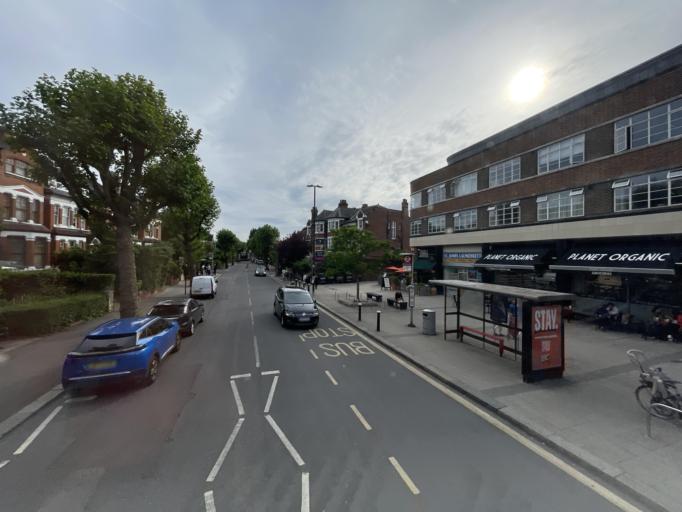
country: GB
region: England
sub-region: Greater London
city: Crouch End
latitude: 51.5893
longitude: -0.1455
